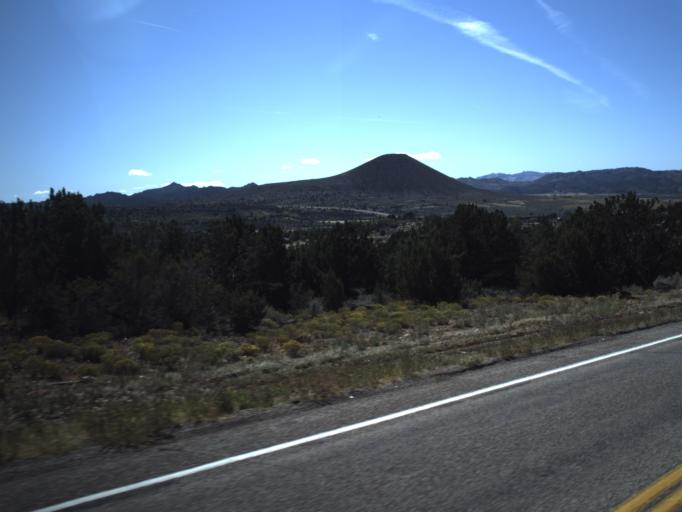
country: US
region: Utah
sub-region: Washington County
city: Ivins
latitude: 37.3513
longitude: -113.6866
